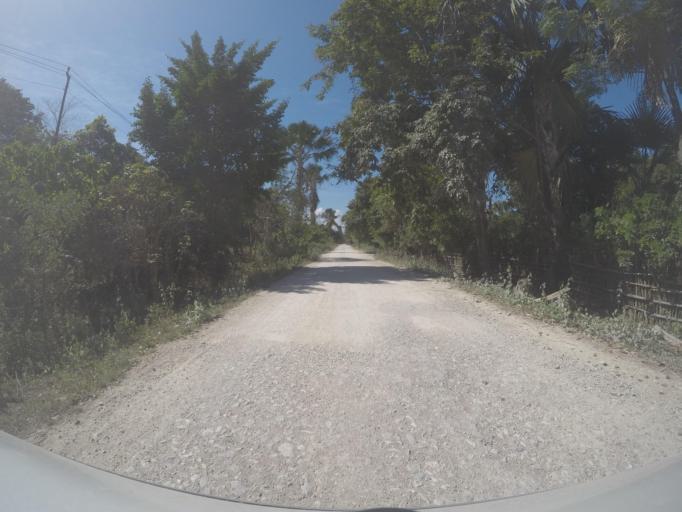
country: TL
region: Viqueque
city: Viqueque
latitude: -8.9070
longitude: 126.5051
